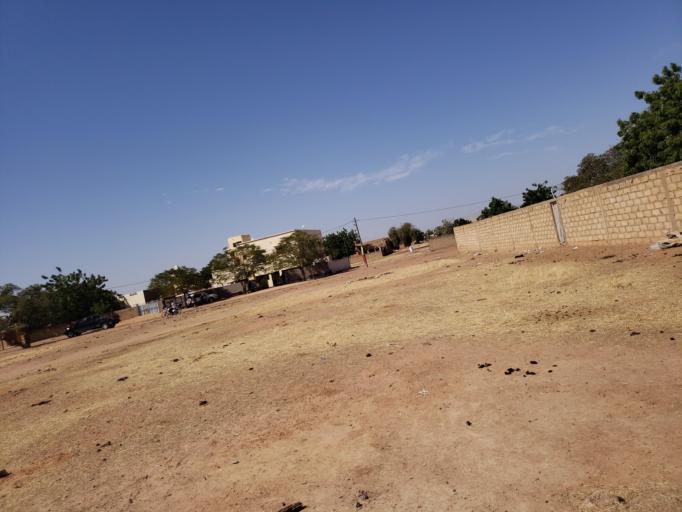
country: SN
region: Matam
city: Ranerou
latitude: 15.2964
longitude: -13.9645
